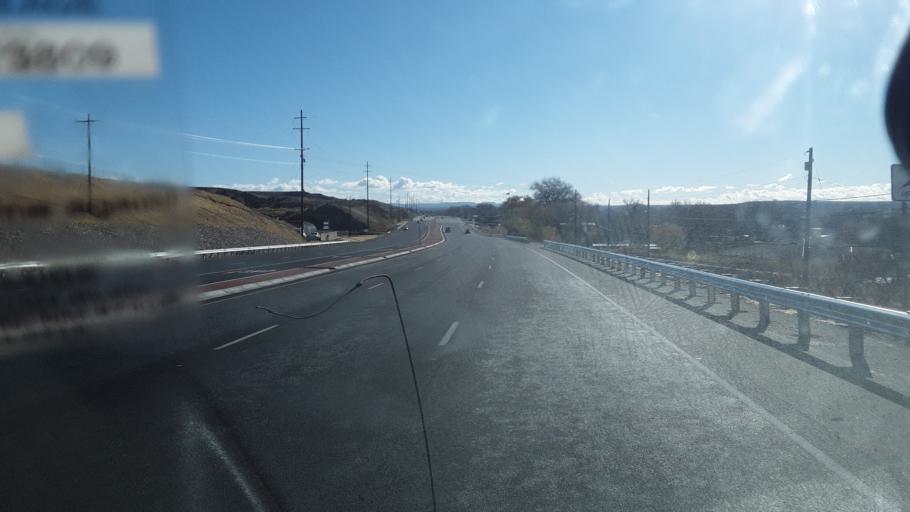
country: US
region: New Mexico
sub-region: San Juan County
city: Farmington
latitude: 36.7119
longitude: -108.1426
